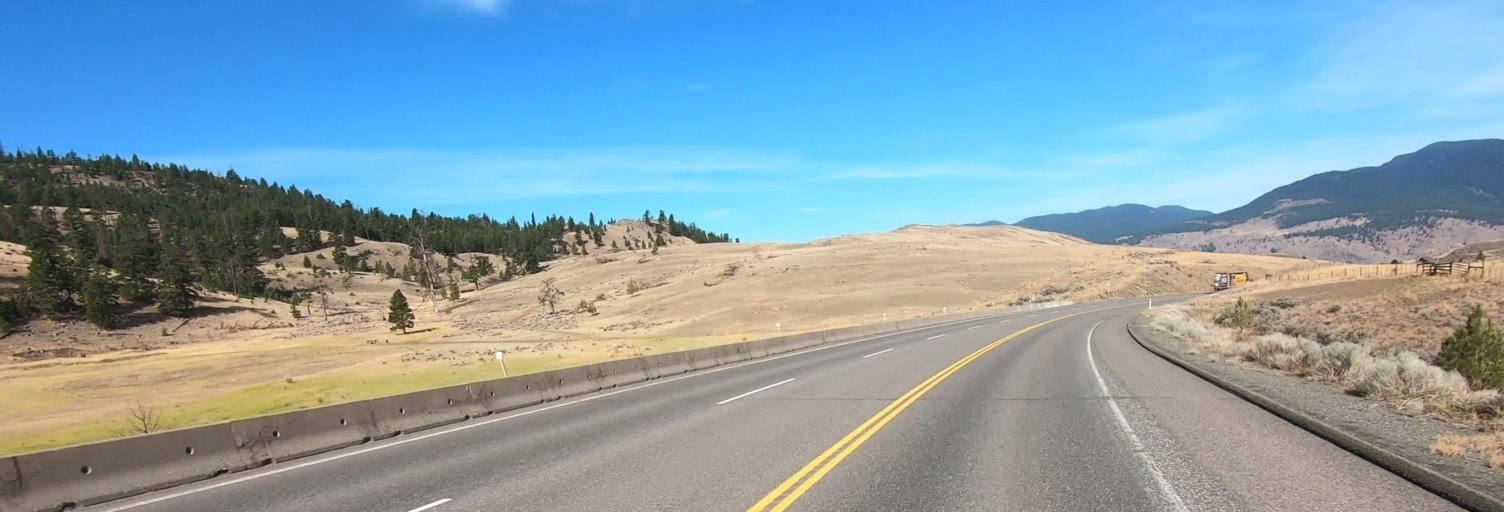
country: CA
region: British Columbia
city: Logan Lake
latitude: 50.7590
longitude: -120.7438
